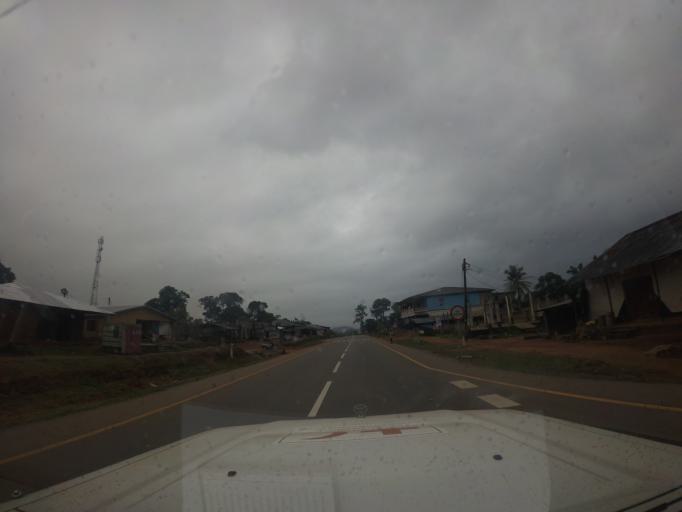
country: SL
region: Eastern Province
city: Hangha
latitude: 7.9389
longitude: -11.1419
